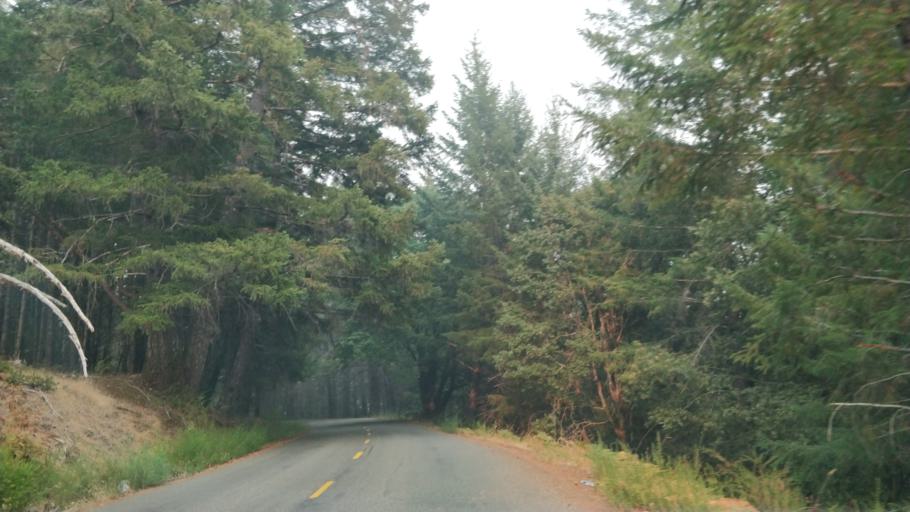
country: US
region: California
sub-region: Humboldt County
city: Rio Dell
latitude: 40.3297
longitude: -124.0346
